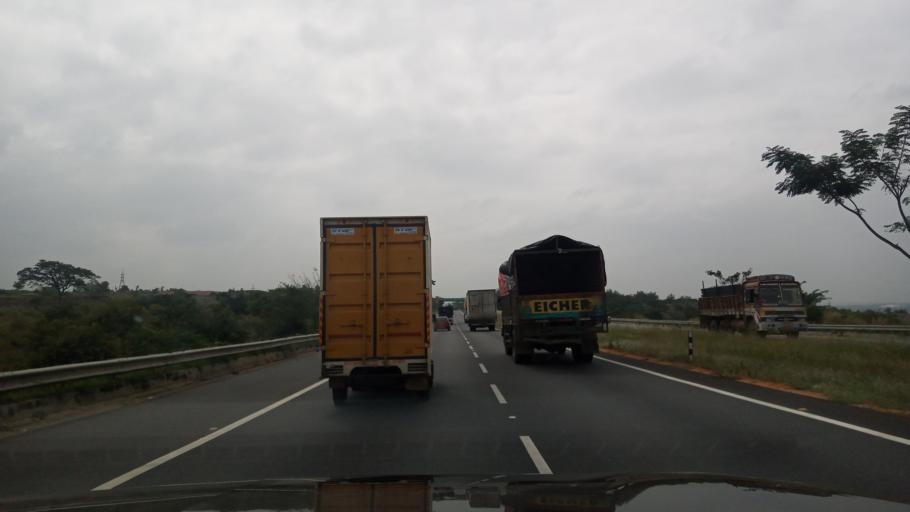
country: IN
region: Karnataka
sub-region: Bangalore Urban
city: Bangalore
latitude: 12.9188
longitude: 77.4687
